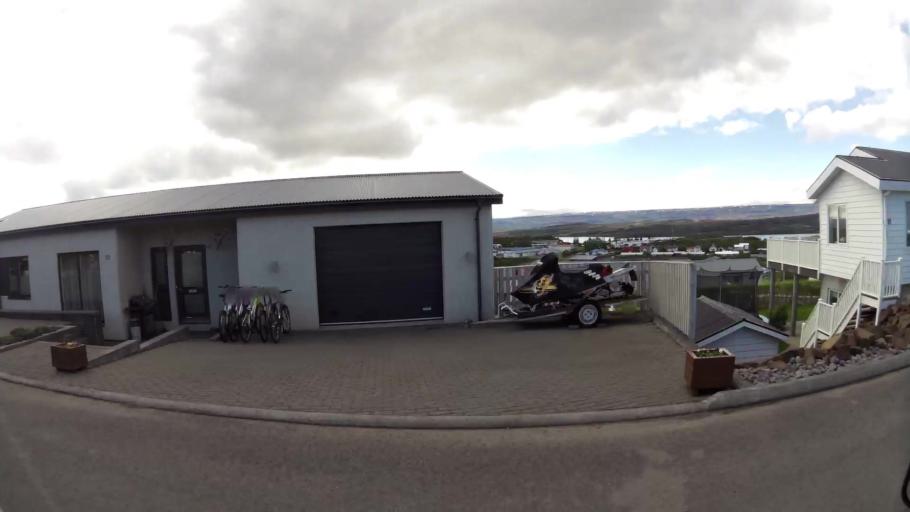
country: IS
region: East
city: Egilsstadir
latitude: 65.2588
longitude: -14.3822
